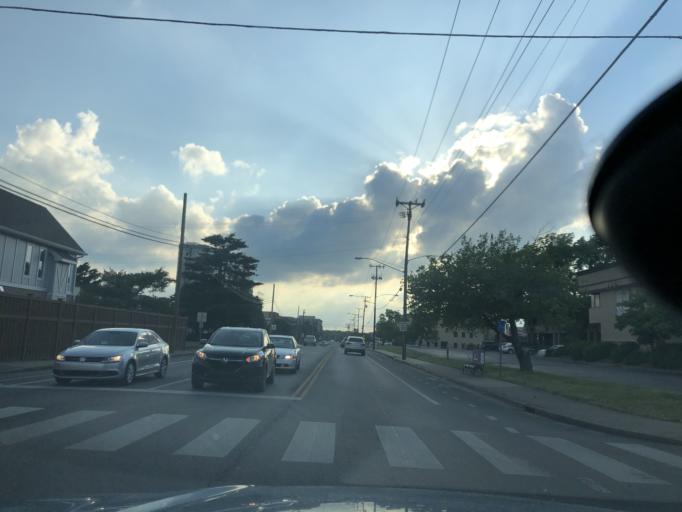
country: US
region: Tennessee
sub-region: Davidson County
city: Oak Hill
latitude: 36.1044
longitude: -86.8089
